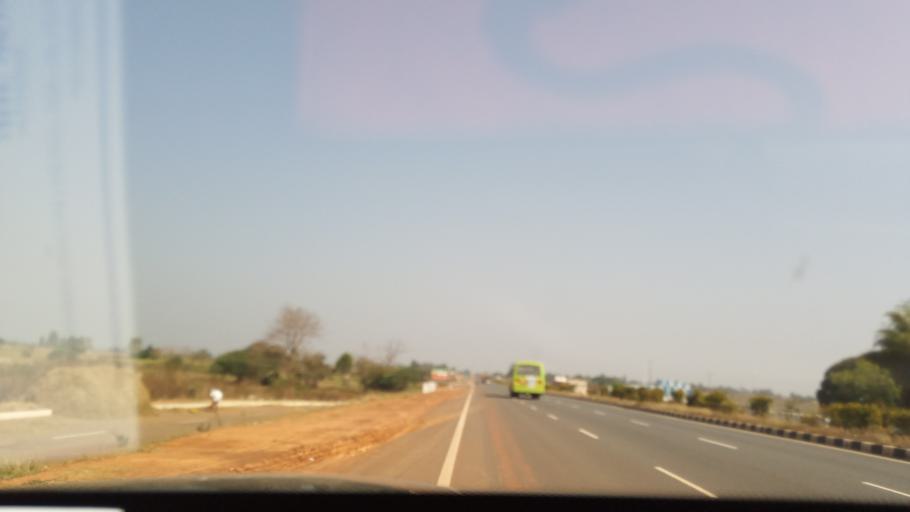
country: IN
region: Karnataka
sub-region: Haveri
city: Shiggaon
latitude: 15.0894
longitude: 75.1522
